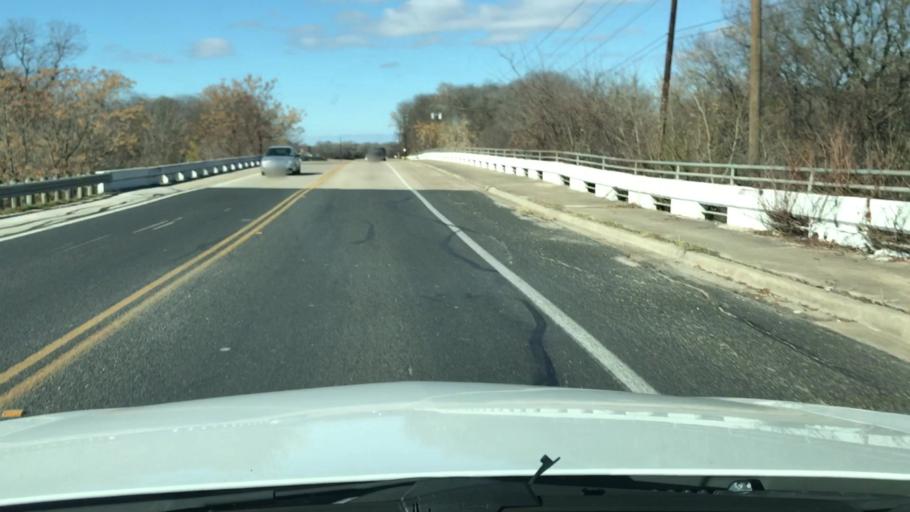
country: US
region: Texas
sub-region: Travis County
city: Onion Creek
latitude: 30.1652
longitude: -97.7337
